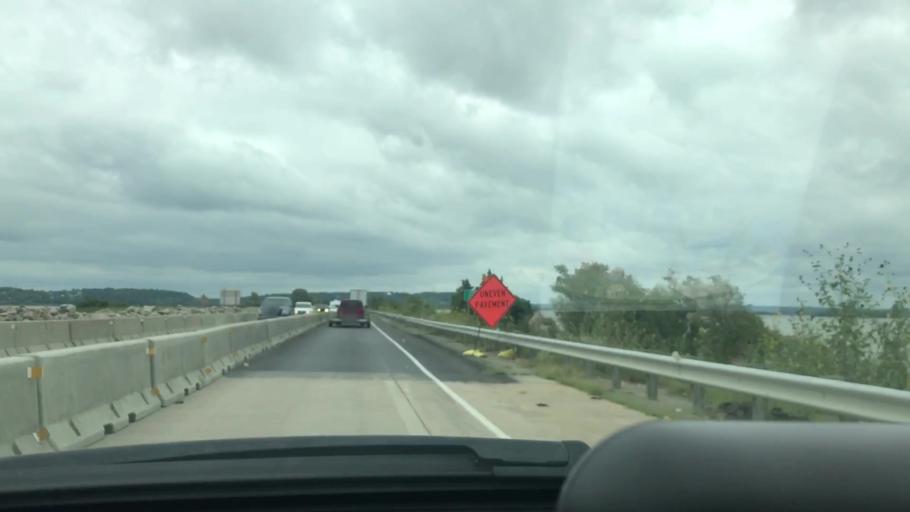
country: US
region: Oklahoma
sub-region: McIntosh County
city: Eufaula
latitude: 35.2265
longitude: -95.6019
